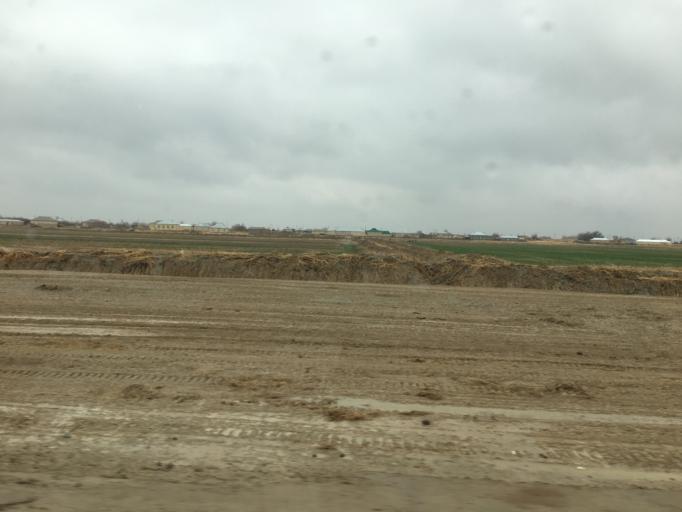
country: TM
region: Mary
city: Yoloeten
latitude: 37.3988
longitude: 62.1780
